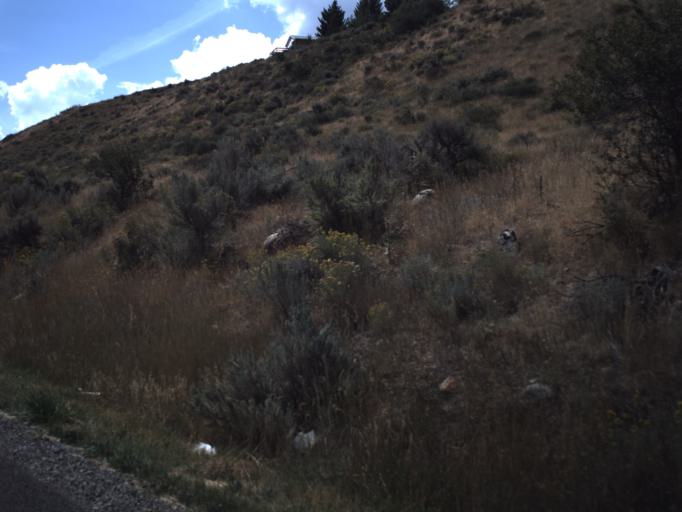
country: US
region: Utah
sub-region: Rich County
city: Randolph
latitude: 41.8925
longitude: -111.3665
